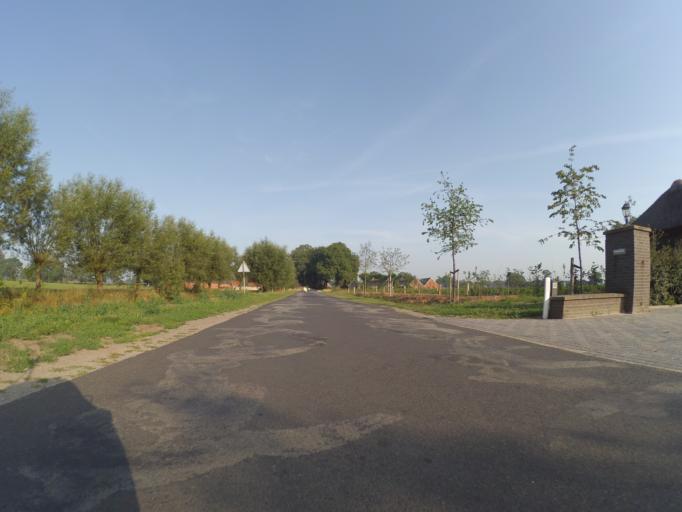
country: NL
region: Overijssel
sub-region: Gemeente Wierden
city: Wierden
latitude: 52.3321
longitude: 6.5336
